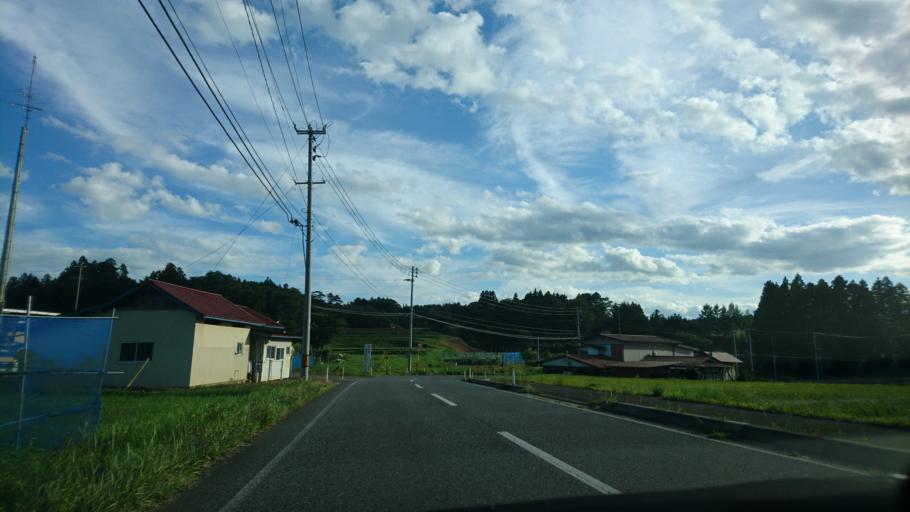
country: JP
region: Iwate
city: Ichinoseki
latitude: 38.8675
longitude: 141.1960
